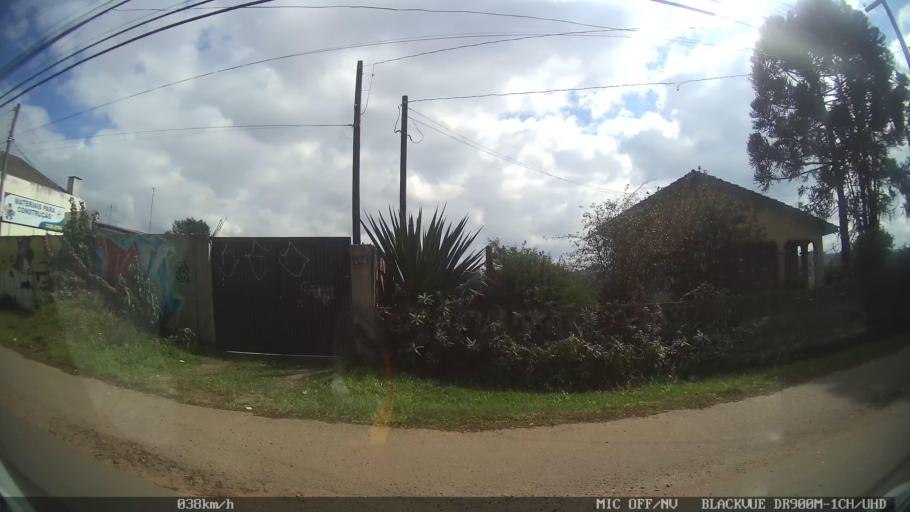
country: BR
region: Parana
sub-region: Colombo
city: Colombo
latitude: -25.3662
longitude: -49.2159
